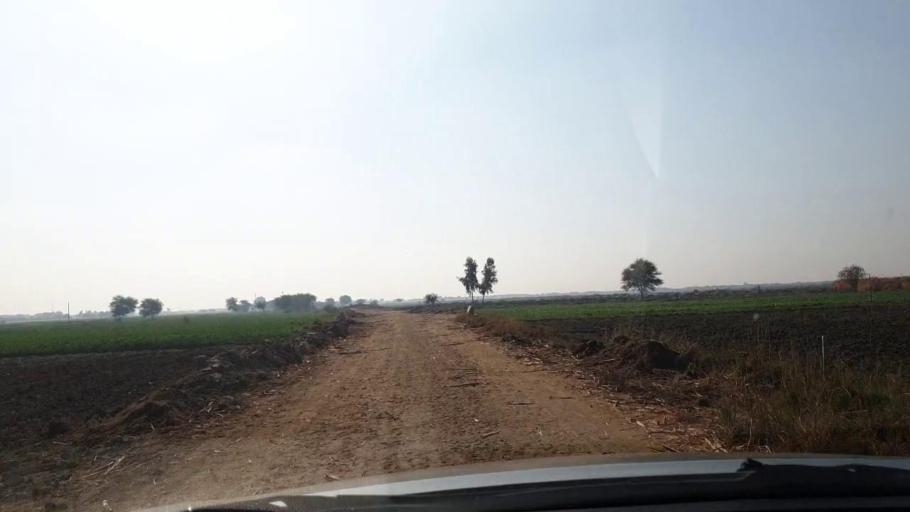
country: PK
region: Sindh
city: Berani
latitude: 25.8297
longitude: 68.9293
